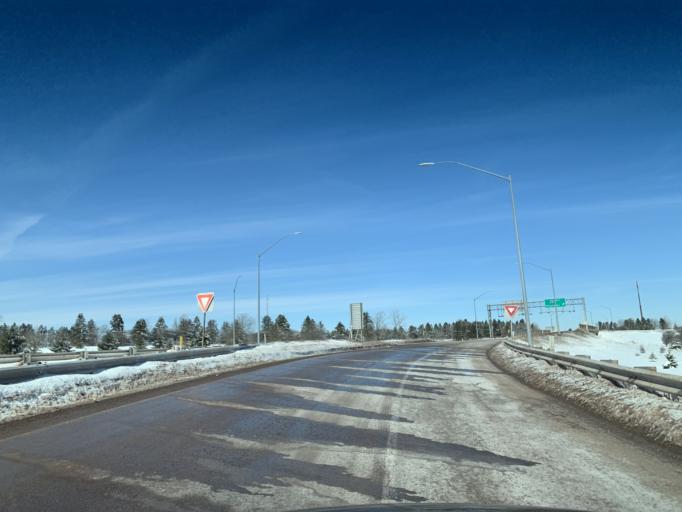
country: US
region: Pennsylvania
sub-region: Somerset County
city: Meyersdale
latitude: 39.6880
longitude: -79.2504
